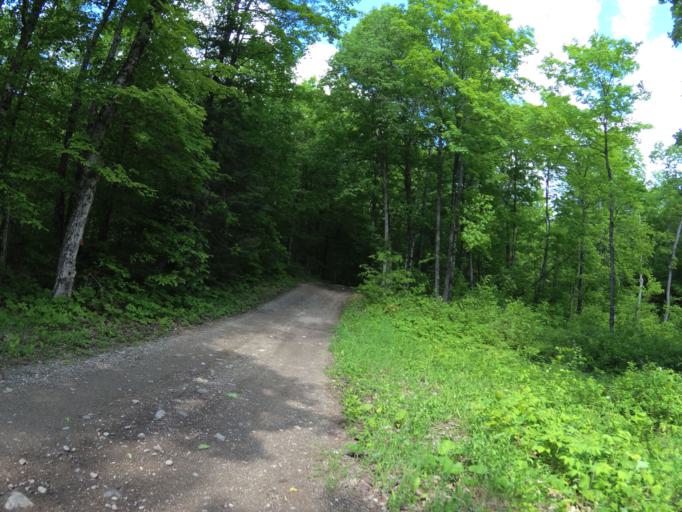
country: CA
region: Ontario
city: Renfrew
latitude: 45.0808
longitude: -76.7680
